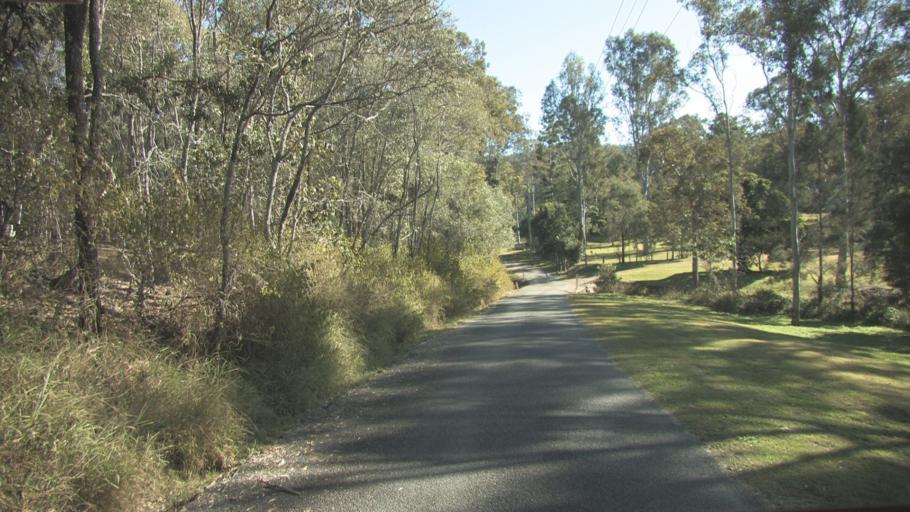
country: AU
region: Queensland
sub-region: Logan
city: Windaroo
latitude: -27.7951
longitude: 153.1739
